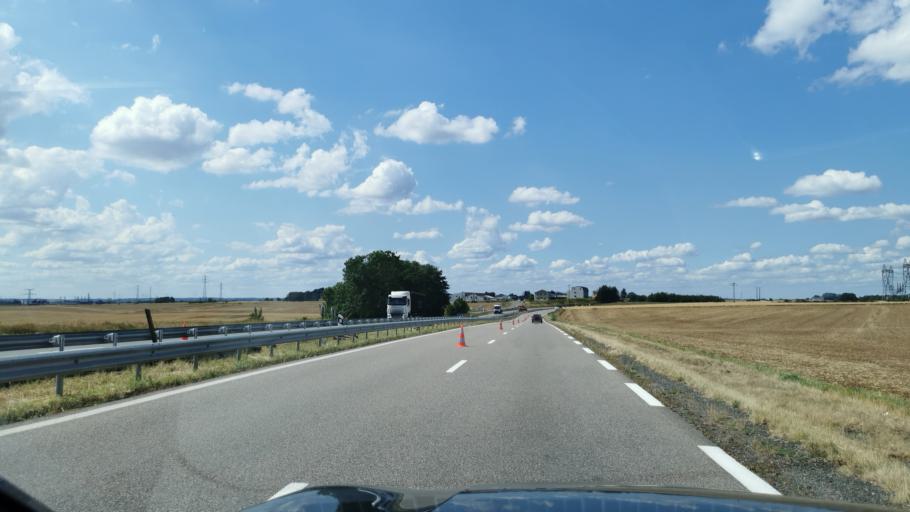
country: FR
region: Lorraine
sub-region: Departement de Meurthe-et-Moselle
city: Villers-la-Montagne
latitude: 49.4812
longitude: 5.8199
